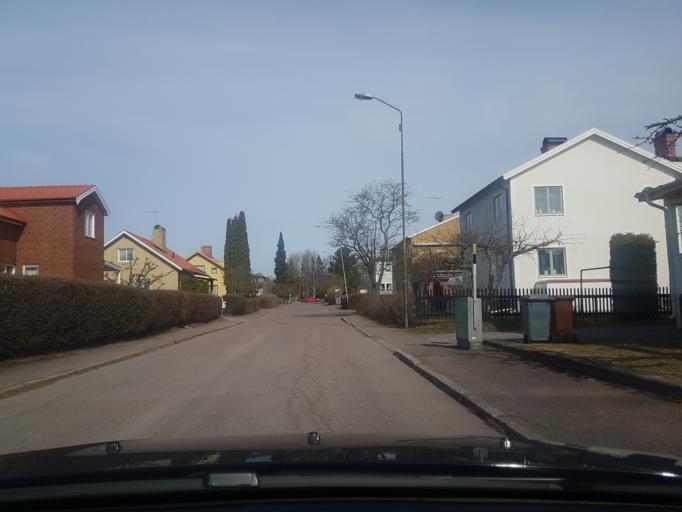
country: SE
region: Dalarna
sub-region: Borlange Kommun
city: Borlaenge
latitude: 60.4909
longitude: 15.4160
